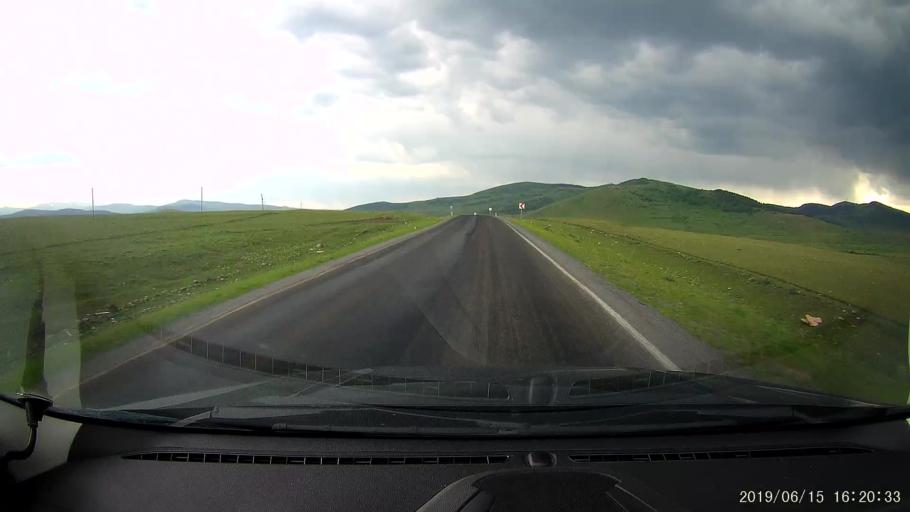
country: TR
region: Ardahan
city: Hanak
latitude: 41.2124
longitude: 42.8471
